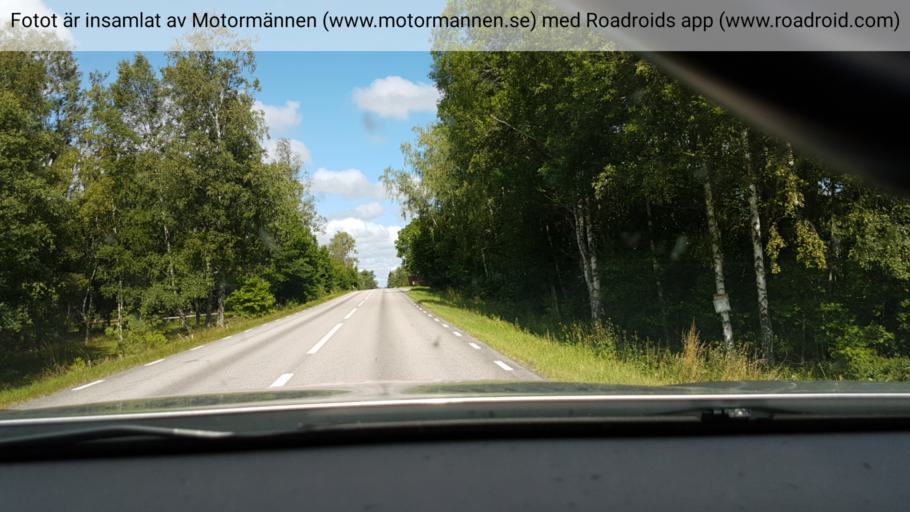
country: SE
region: Stockholm
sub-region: Norrtalje Kommun
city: Arno
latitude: 59.9945
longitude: 18.8055
